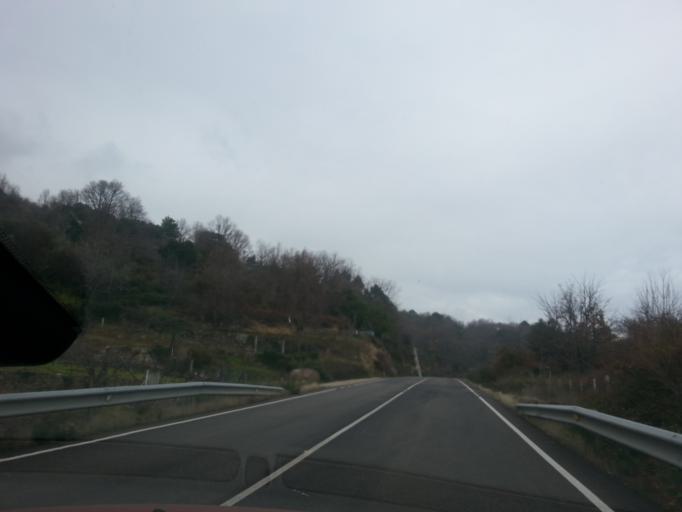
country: ES
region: Castille and Leon
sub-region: Provincia de Salamanca
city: Madronal
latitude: 40.4538
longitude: -6.0667
